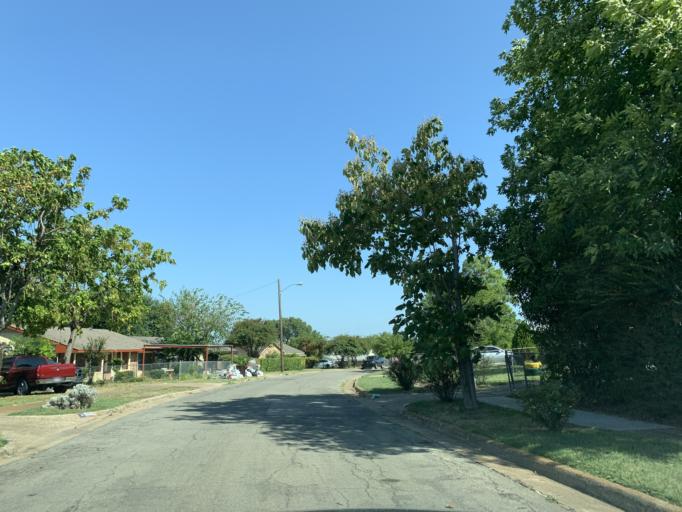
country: US
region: Texas
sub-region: Dallas County
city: Hutchins
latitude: 32.6655
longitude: -96.7475
